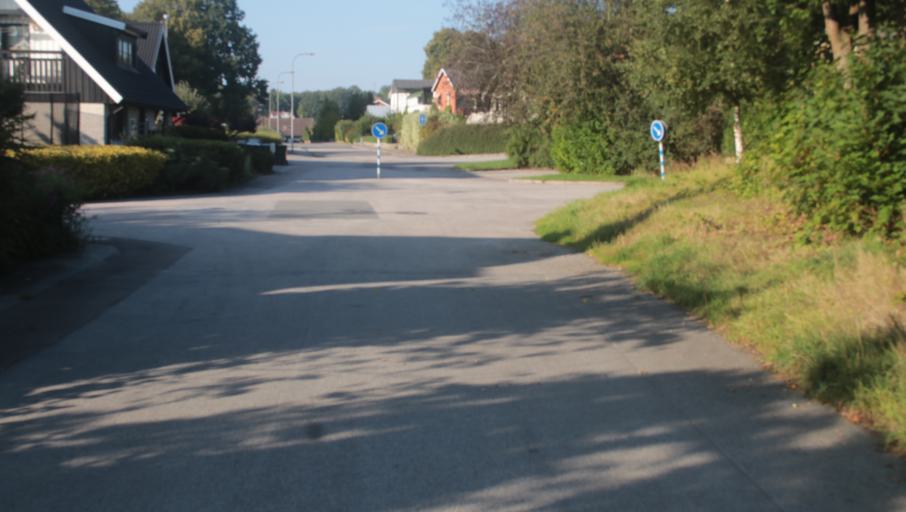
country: SE
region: Blekinge
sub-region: Karlshamns Kommun
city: Karlshamn
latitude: 56.1820
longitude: 14.8585
